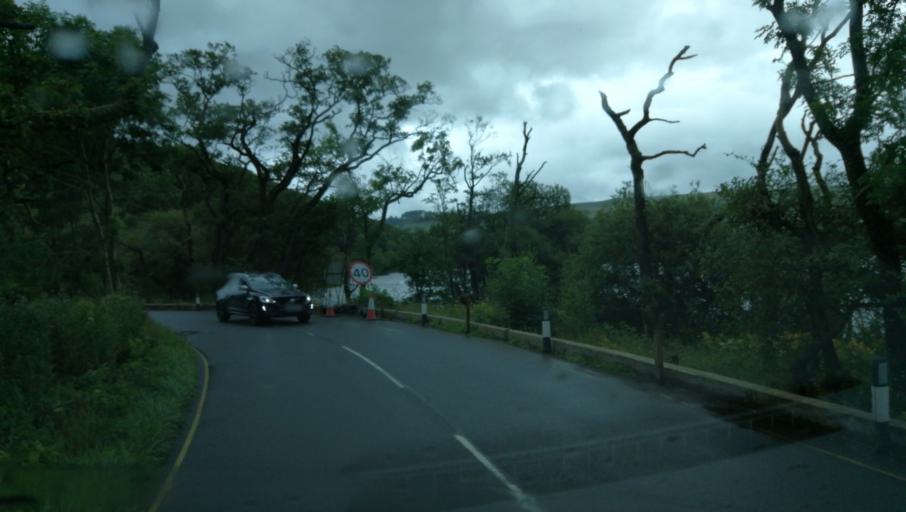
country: GB
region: England
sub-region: Cumbria
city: Penrith
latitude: 54.6106
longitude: -2.8340
